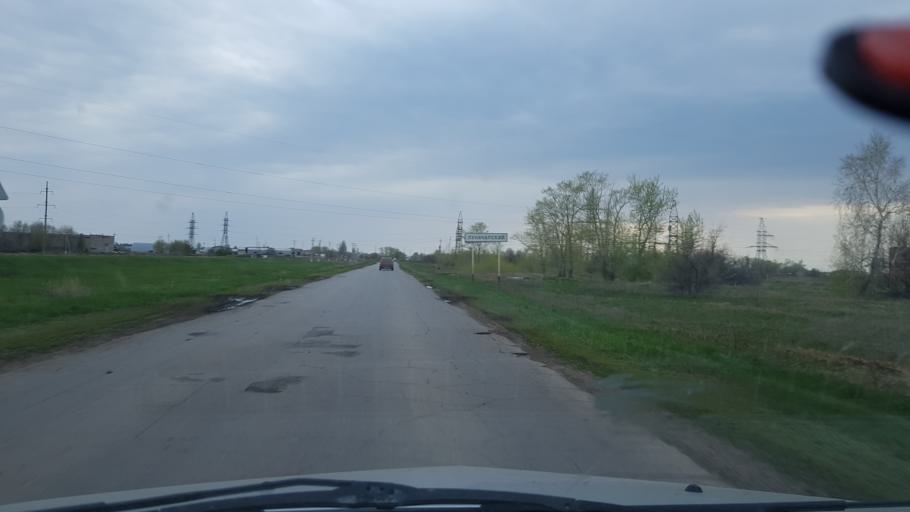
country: RU
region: Samara
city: Khryashchevka
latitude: 53.6719
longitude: 49.0918
